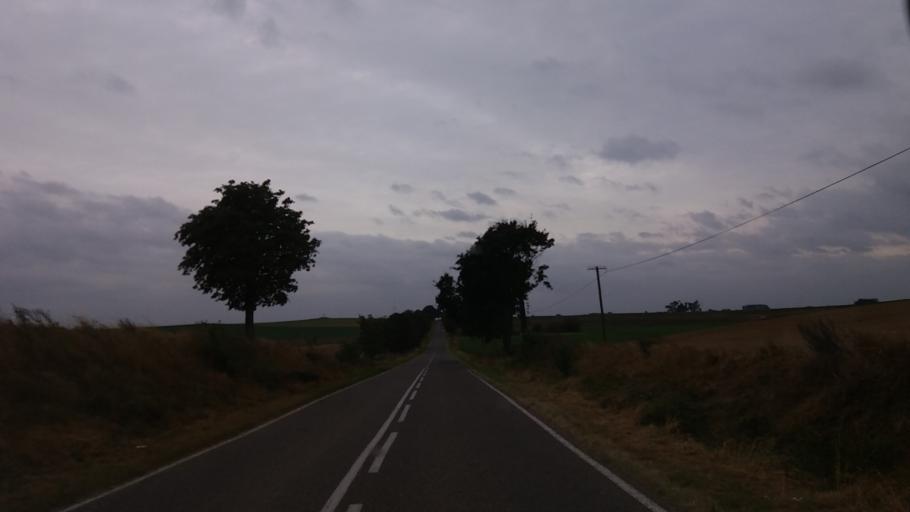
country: PL
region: Lubusz
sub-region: Powiat strzelecko-drezdenecki
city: Strzelce Krajenskie
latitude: 52.9439
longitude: 15.5639
